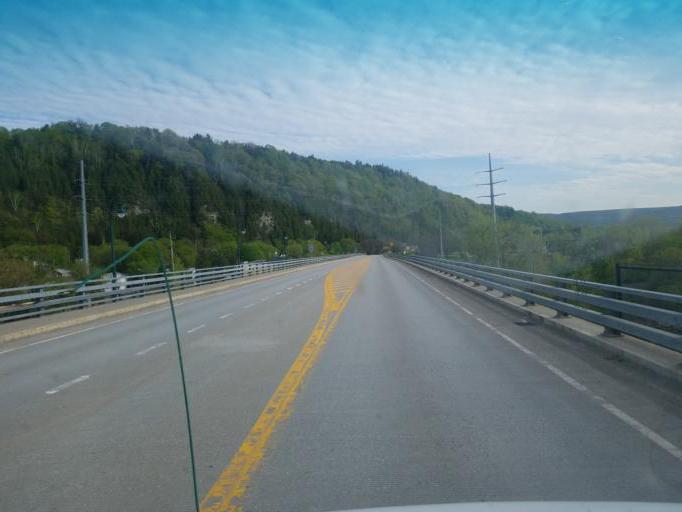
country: US
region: New York
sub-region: Herkimer County
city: Little Falls
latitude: 43.0405
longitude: -74.8606
